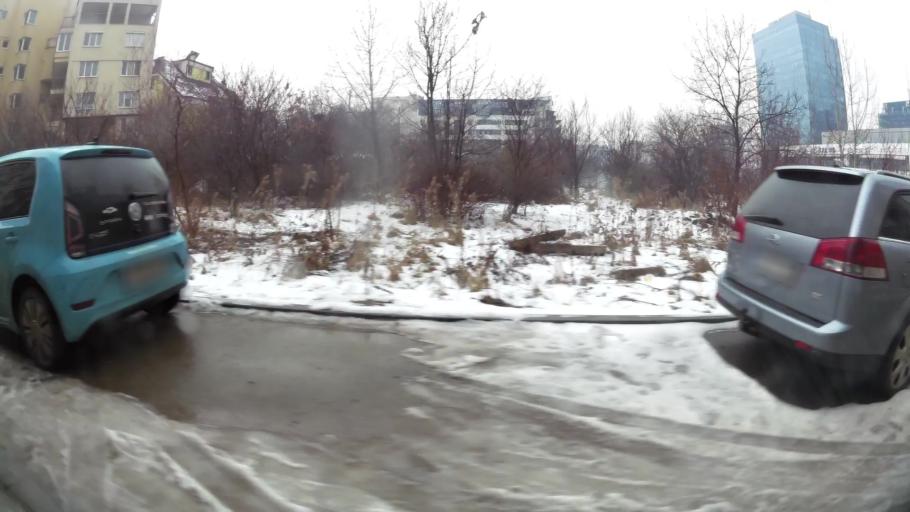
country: BG
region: Sofia-Capital
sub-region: Stolichna Obshtina
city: Sofia
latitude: 42.6622
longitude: 23.2885
